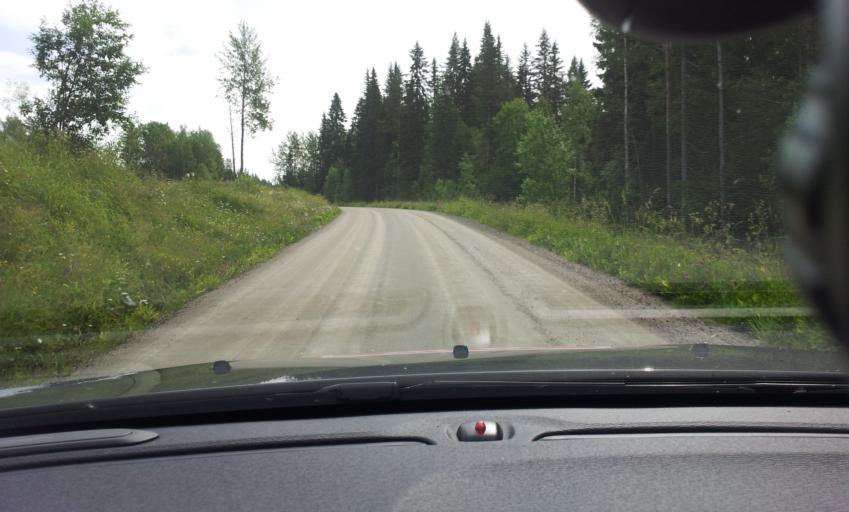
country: SE
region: Jaemtland
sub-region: OEstersunds Kommun
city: Brunflo
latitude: 62.9401
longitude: 14.9588
